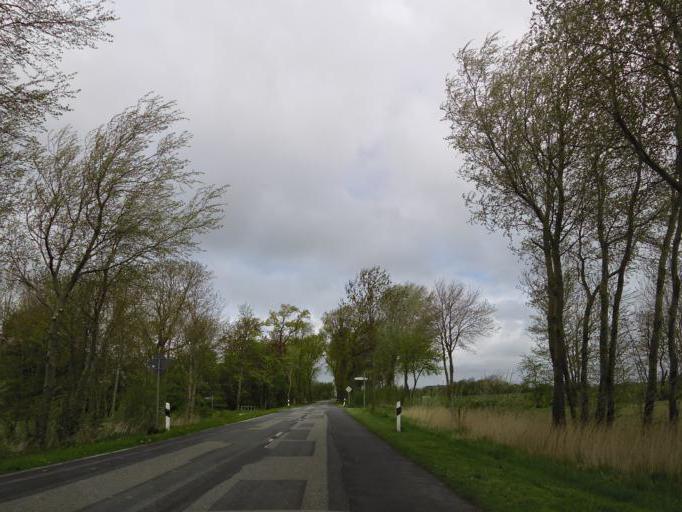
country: DE
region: Schleswig-Holstein
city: Galmsbull
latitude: 54.7678
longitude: 8.7515
